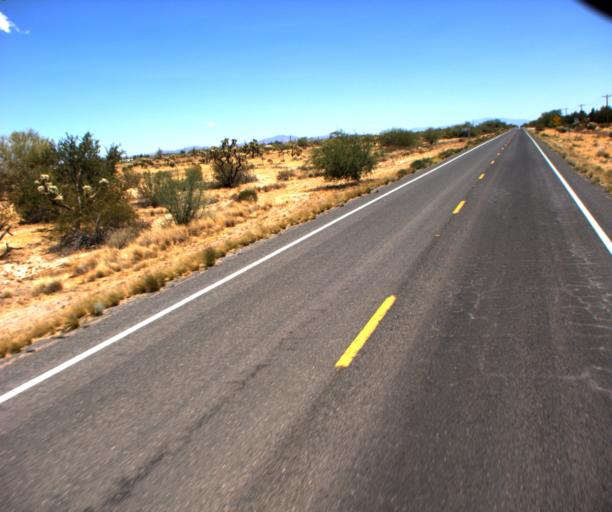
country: US
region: Arizona
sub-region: Pinal County
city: Florence
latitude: 32.9518
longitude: -111.3273
